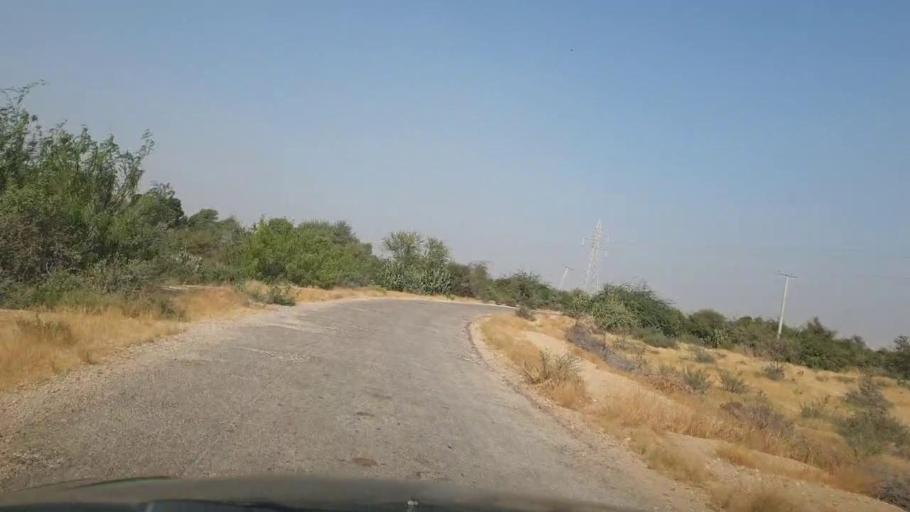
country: PK
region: Sindh
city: Jamshoro
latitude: 25.5287
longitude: 67.8218
